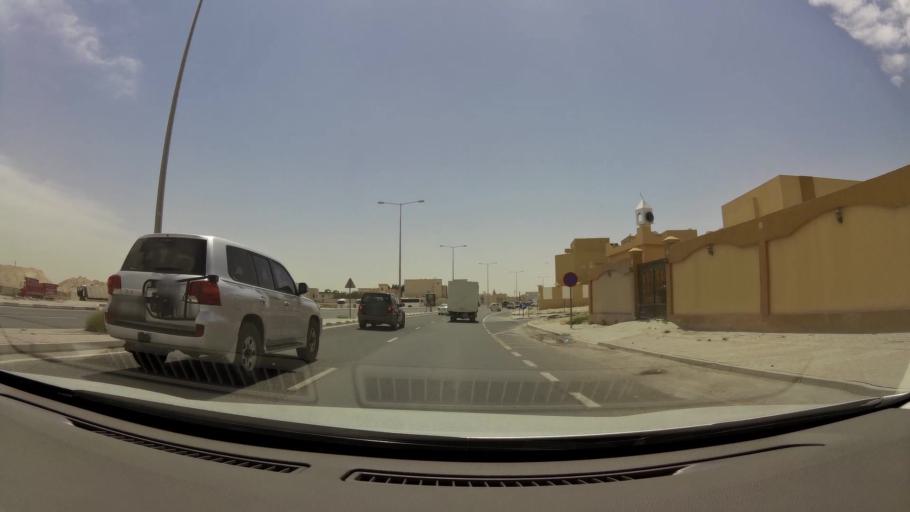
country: QA
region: Baladiyat ar Rayyan
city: Ar Rayyan
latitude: 25.2640
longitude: 51.4205
